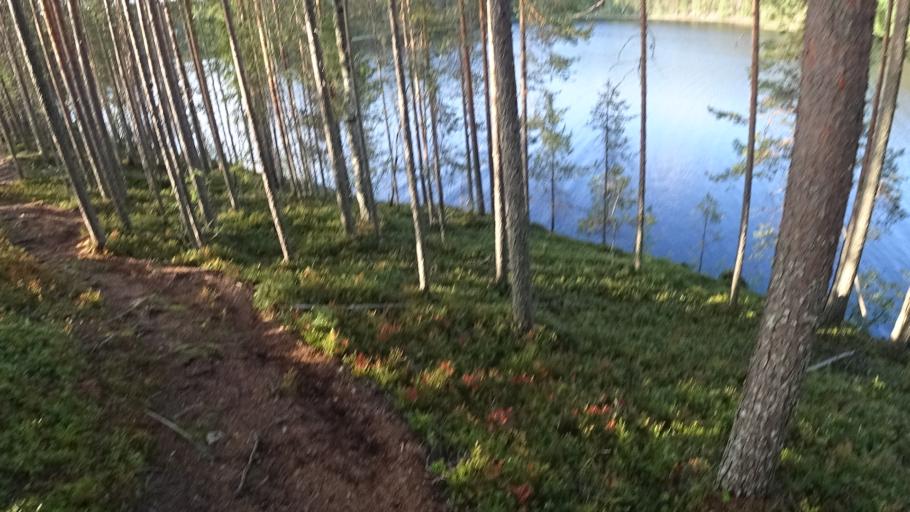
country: FI
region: North Karelia
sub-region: Joensuu
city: Ilomantsi
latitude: 62.5774
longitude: 31.1716
